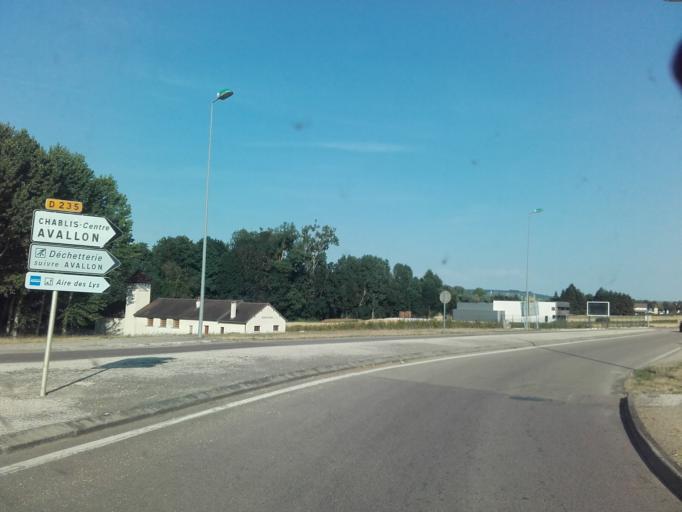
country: FR
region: Bourgogne
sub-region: Departement de l'Yonne
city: Chablis
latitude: 47.8196
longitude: 3.7786
